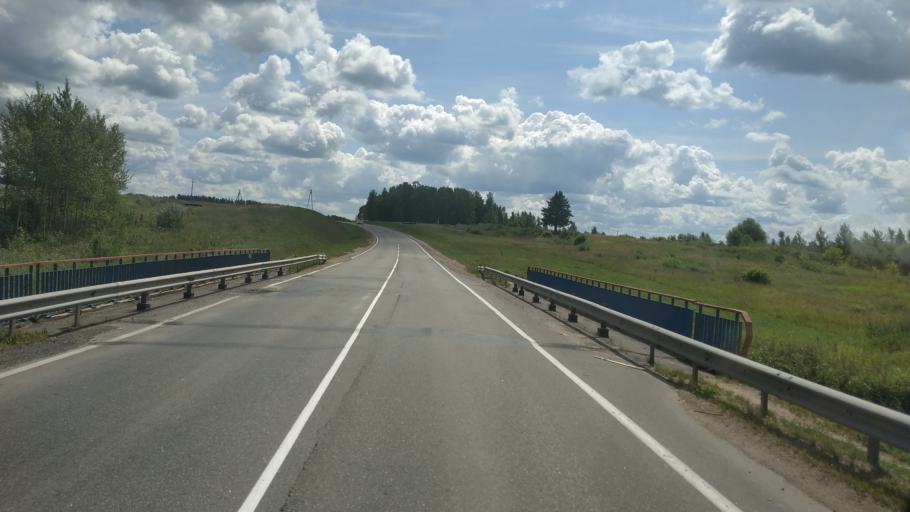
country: BY
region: Mogilev
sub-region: Mahilyowski Rayon
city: Veyno
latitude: 53.8357
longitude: 30.4000
